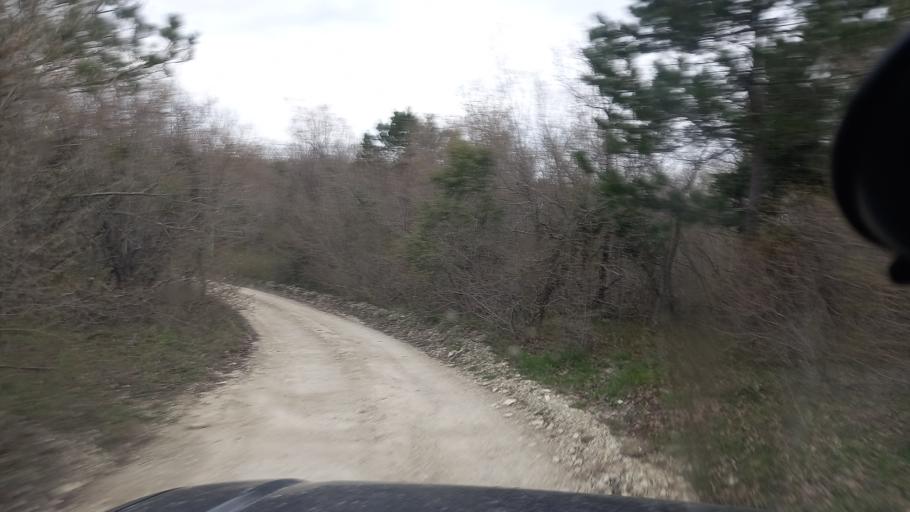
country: RU
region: Krasnodarskiy
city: Dzhubga
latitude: 44.3225
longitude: 38.6881
